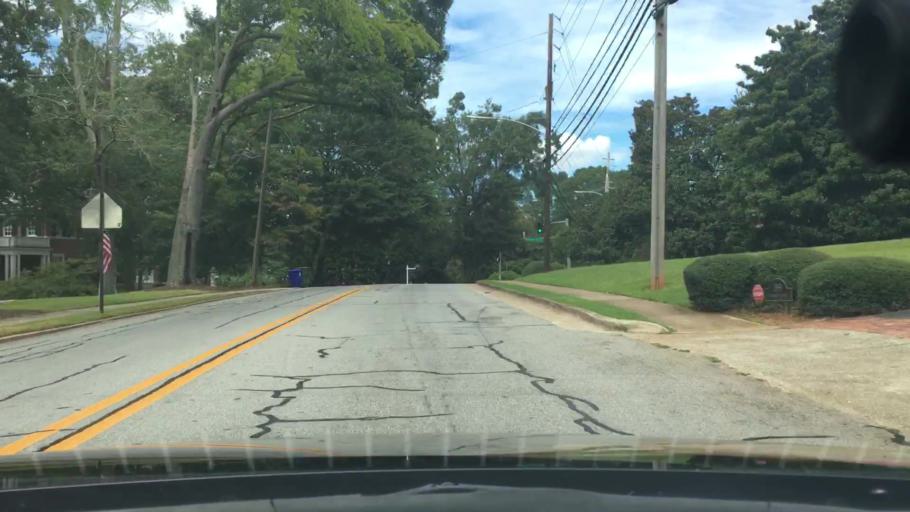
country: US
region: Georgia
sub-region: Coweta County
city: Newnan
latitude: 33.3891
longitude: -84.8013
